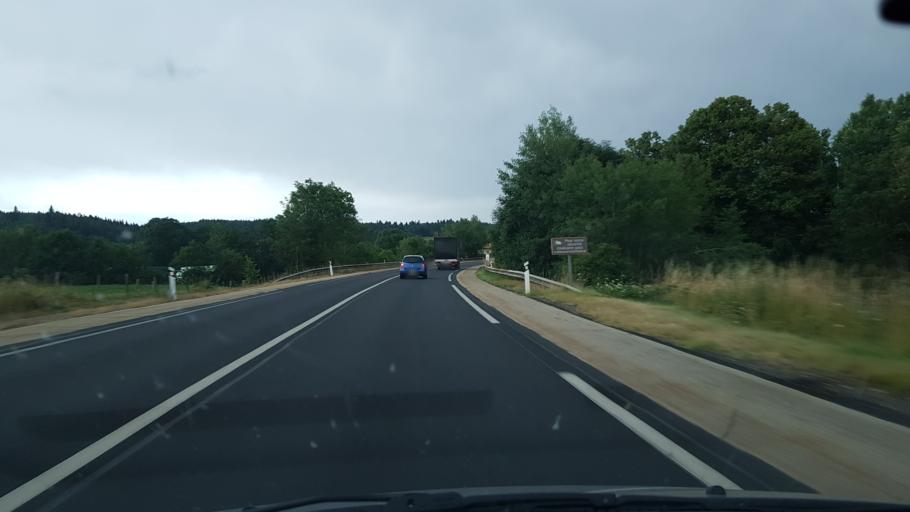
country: FR
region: Auvergne
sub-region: Departement de la Haute-Loire
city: Allegre
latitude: 45.1390
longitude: 3.6265
